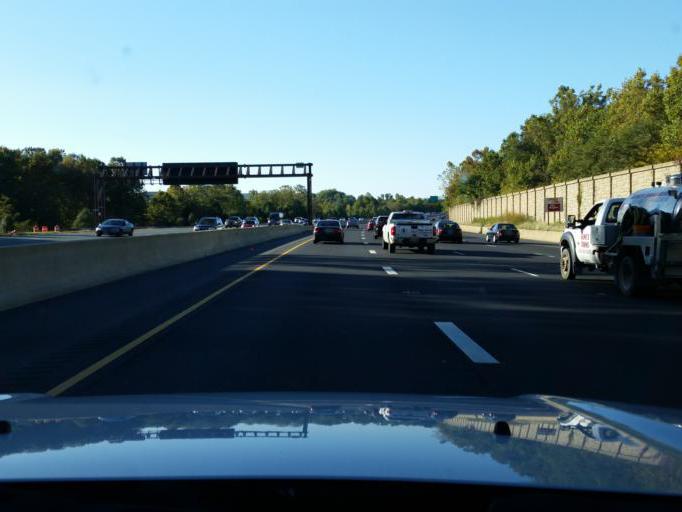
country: US
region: Maryland
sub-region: Montgomery County
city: Germantown
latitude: 39.1642
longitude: -77.2385
